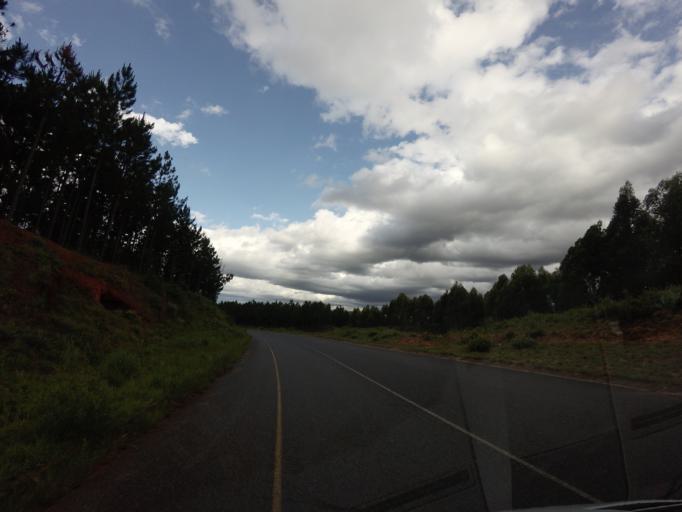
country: ZA
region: Mpumalanga
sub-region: Ehlanzeni District
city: Graksop
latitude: -24.9923
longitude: 31.0069
